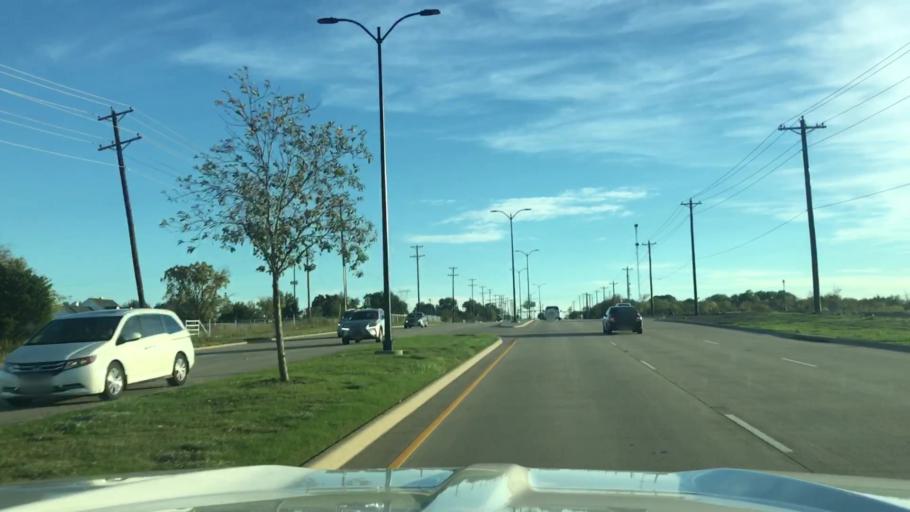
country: US
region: Texas
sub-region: Collin County
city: Prosper
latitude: 33.2099
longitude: -96.8027
